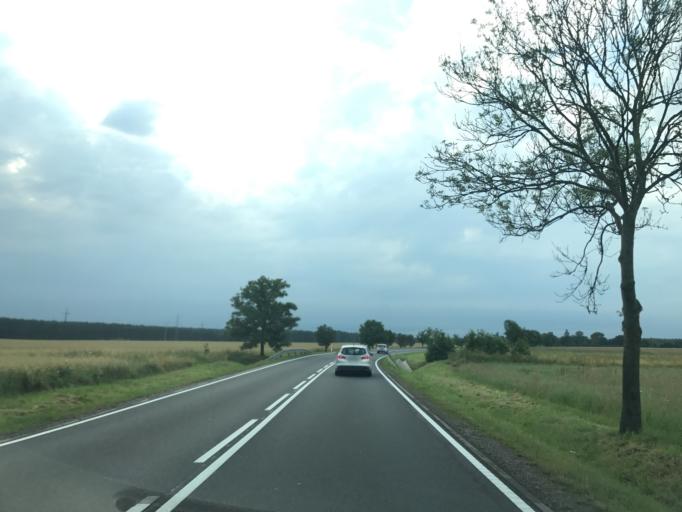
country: PL
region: Pomeranian Voivodeship
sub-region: Powiat czluchowski
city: Rzeczenica
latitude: 53.7416
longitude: 17.1802
